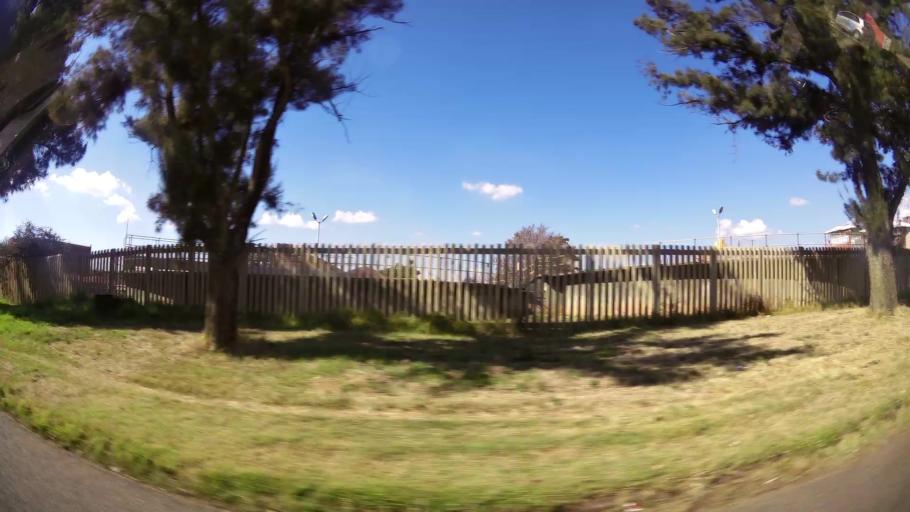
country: ZA
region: Mpumalanga
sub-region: Nkangala District Municipality
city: Witbank
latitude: -25.8821
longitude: 29.2307
